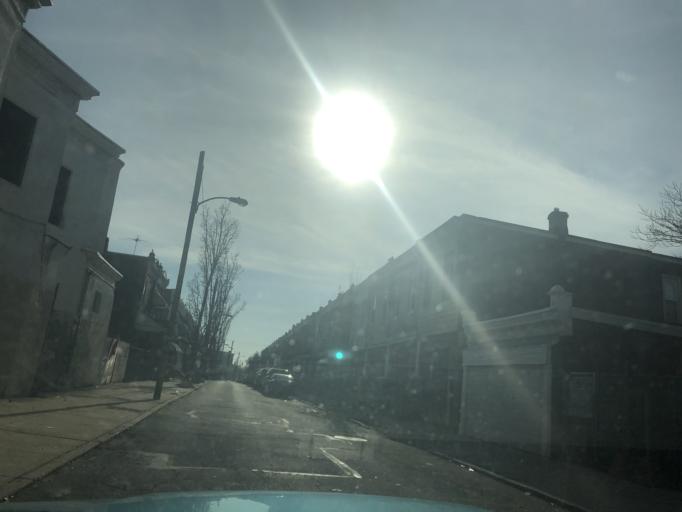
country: US
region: Pennsylvania
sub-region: Delaware County
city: Millbourne
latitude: 39.9694
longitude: -75.2385
